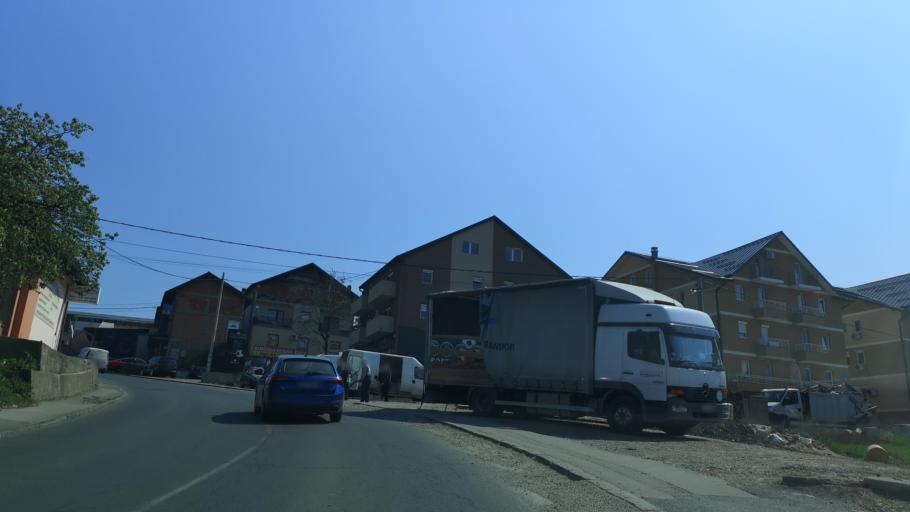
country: RS
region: Central Serbia
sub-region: Belgrade
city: Zvezdara
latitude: 44.7638
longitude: 20.5529
